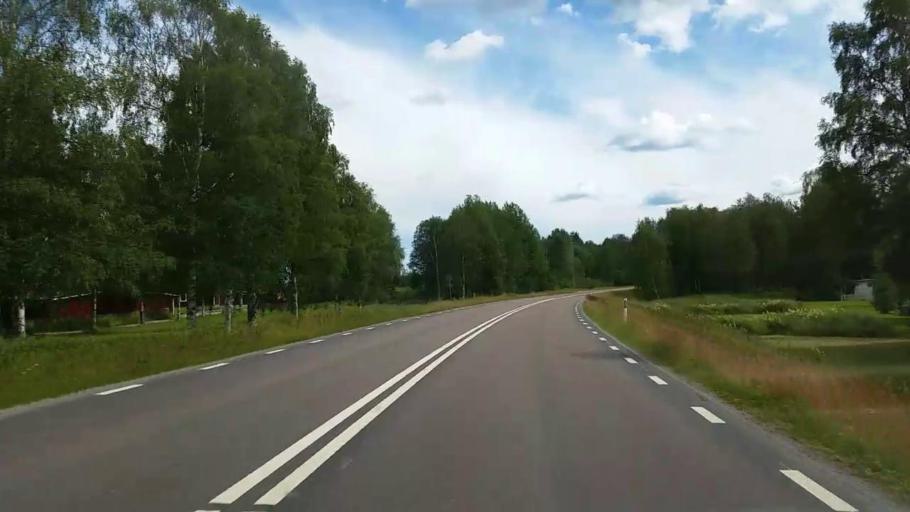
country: SE
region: Gaevleborg
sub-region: Ovanakers Kommun
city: Edsbyn
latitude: 61.3827
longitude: 15.8297
